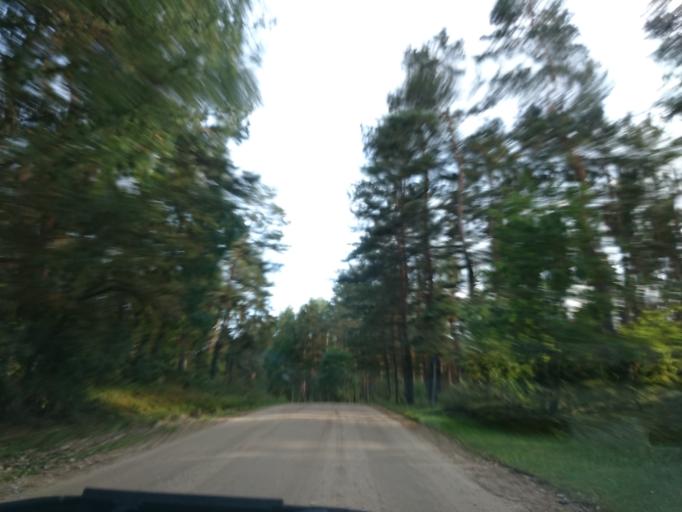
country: LV
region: Adazi
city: Adazi
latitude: 57.0611
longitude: 24.3660
